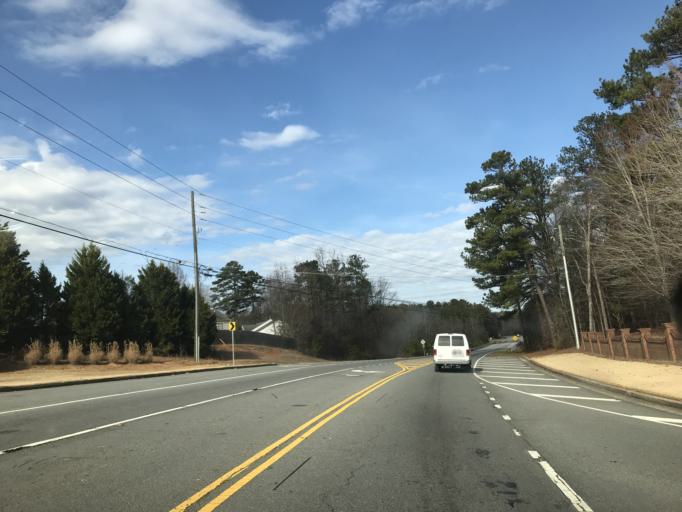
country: US
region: Georgia
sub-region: Douglas County
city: Douglasville
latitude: 33.7938
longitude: -84.8062
